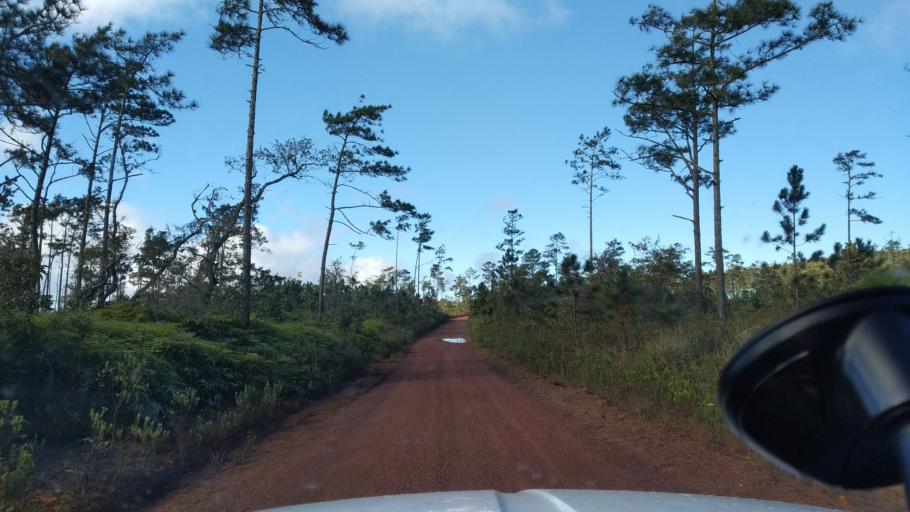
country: BZ
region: Cayo
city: Belmopan
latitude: 16.9983
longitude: -88.8414
